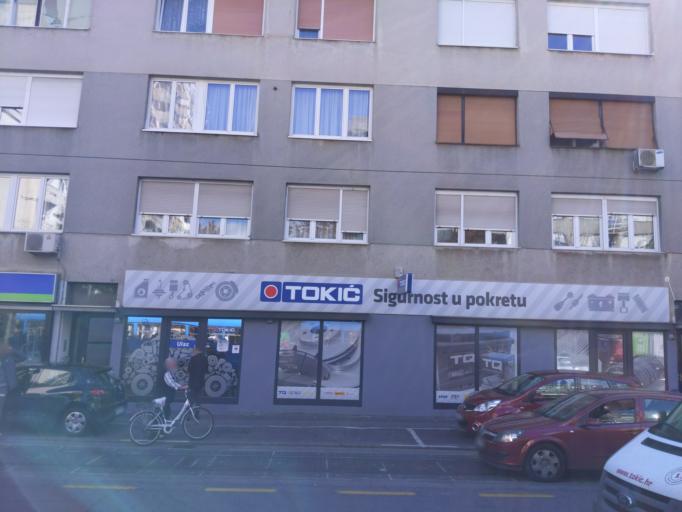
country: HR
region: Grad Zagreb
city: Zagreb
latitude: 45.8171
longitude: 16.0063
